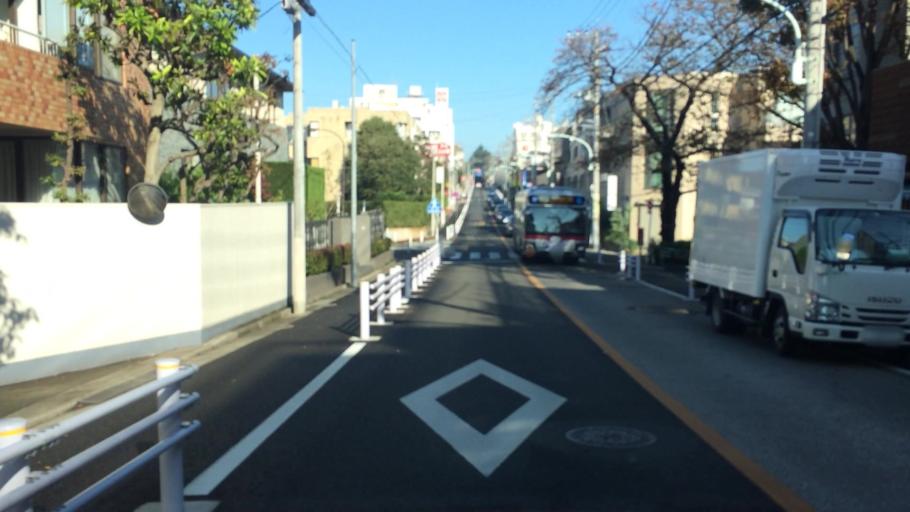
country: JP
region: Tokyo
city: Tokyo
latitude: 35.6208
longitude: 139.6670
